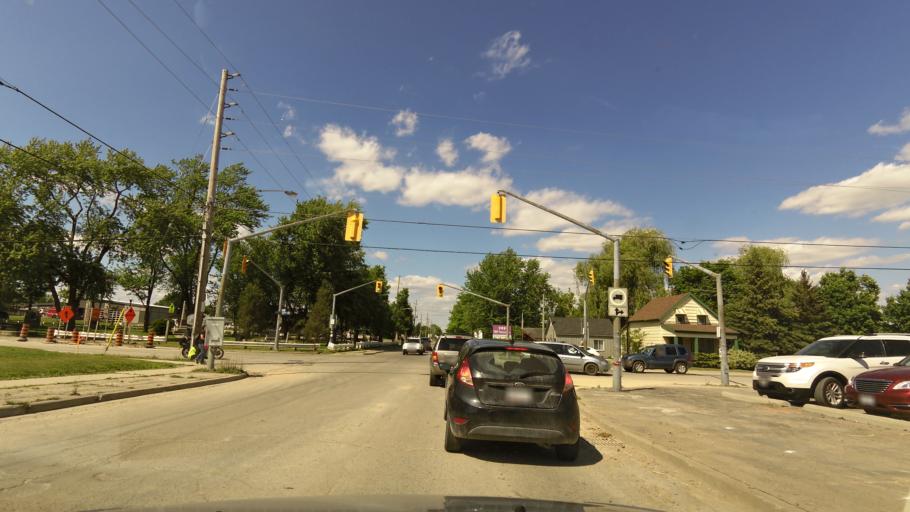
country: CA
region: Ontario
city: Brantford
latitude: 43.0685
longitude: -80.1181
